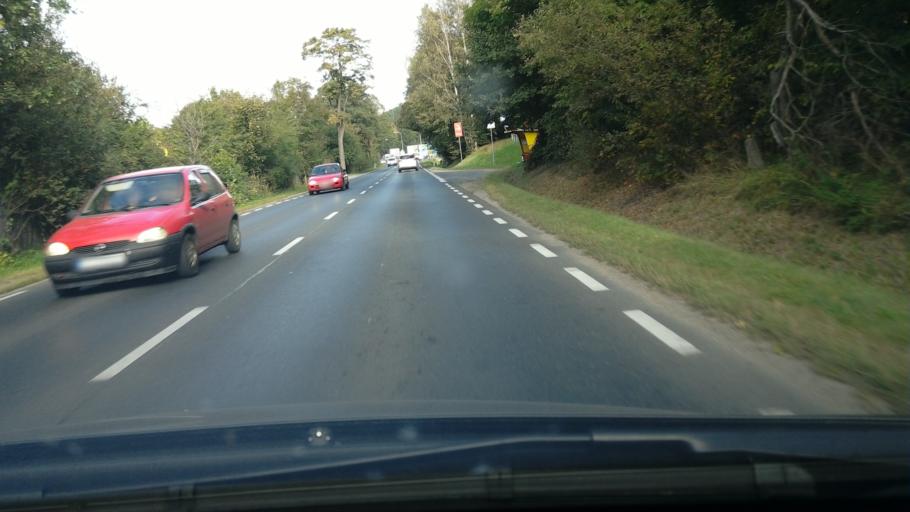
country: PL
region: Lower Silesian Voivodeship
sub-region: Jelenia Gora
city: Jelenia Gora
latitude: 50.8854
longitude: 15.7570
